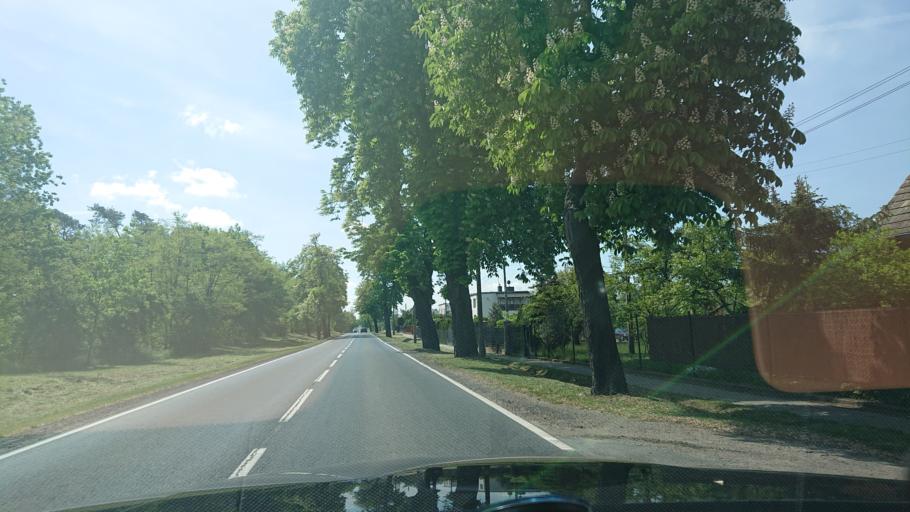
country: PL
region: Greater Poland Voivodeship
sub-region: Powiat gnieznienski
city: Gniezno
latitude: 52.5063
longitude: 17.5948
